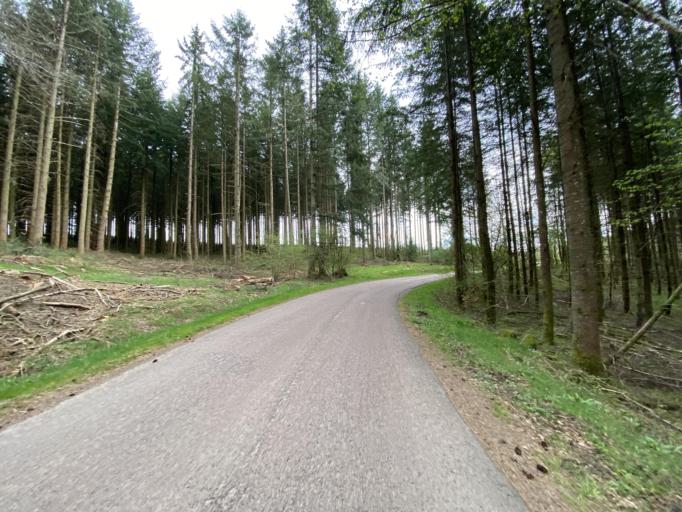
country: FR
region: Bourgogne
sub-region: Departement de la Cote-d'Or
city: Saulieu
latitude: 47.3104
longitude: 4.0896
